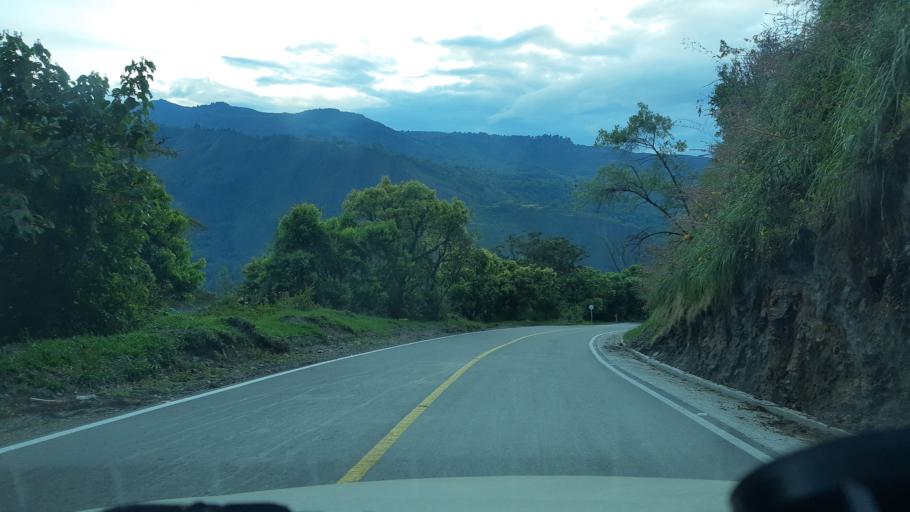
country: CO
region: Boyaca
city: Chivor
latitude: 4.9778
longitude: -73.3333
